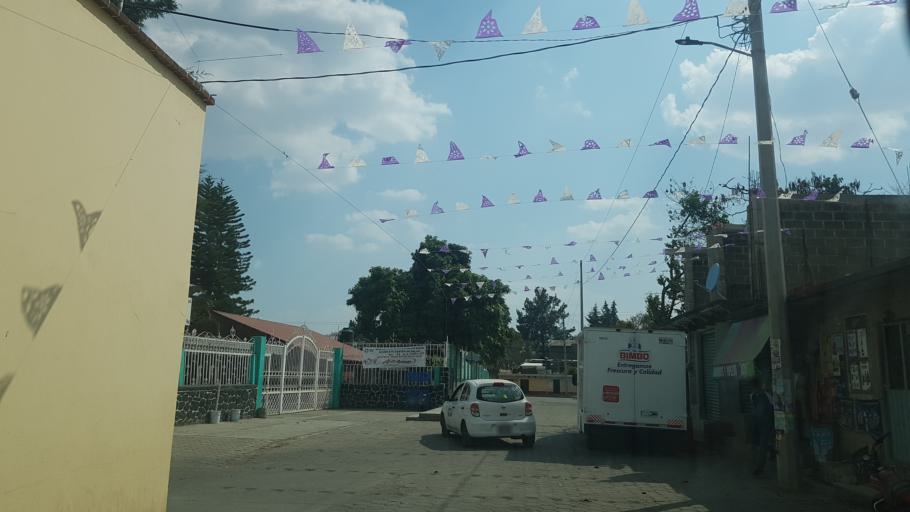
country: MX
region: Puebla
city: San Juan Amecac
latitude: 18.8332
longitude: -98.6608
